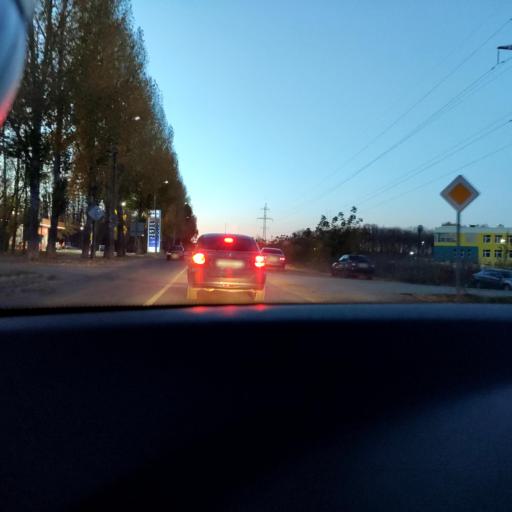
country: RU
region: Samara
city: Petra-Dubrava
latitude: 53.3054
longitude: 50.2803
